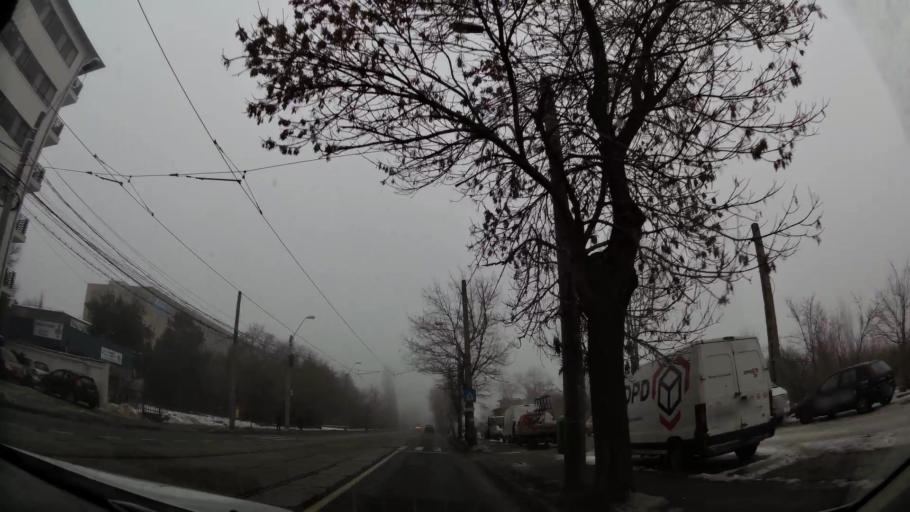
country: RO
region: Ilfov
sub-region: Comuna Chiajna
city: Rosu
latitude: 44.4687
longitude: 26.0280
